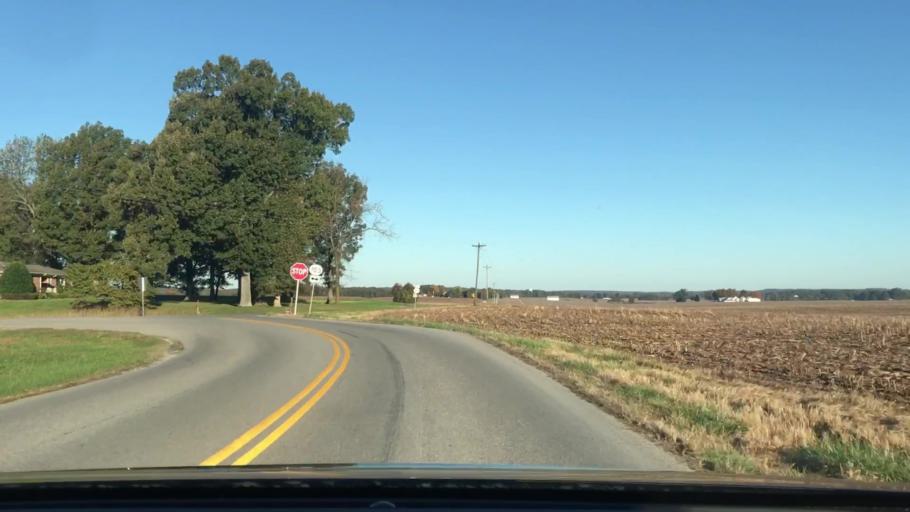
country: US
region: Kentucky
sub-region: Logan County
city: Auburn
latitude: 36.8312
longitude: -86.6836
